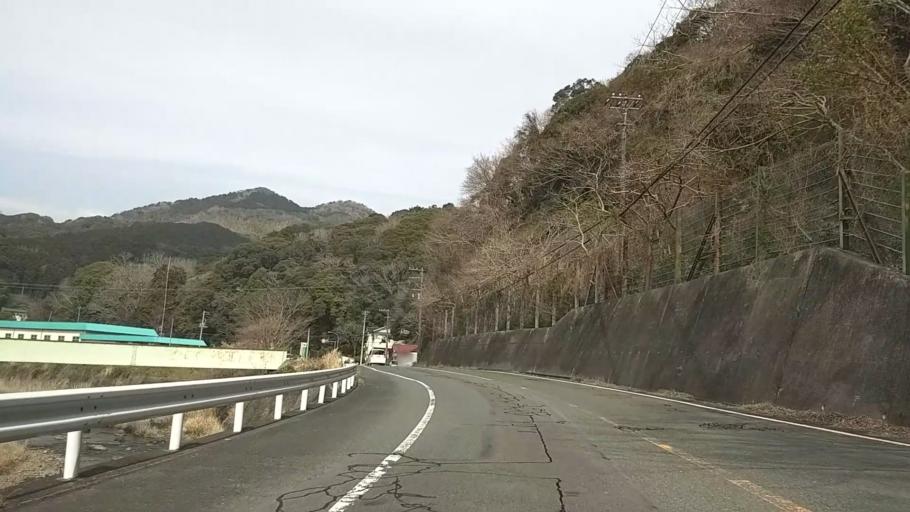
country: JP
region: Shizuoka
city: Shimoda
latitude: 34.7204
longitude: 138.9465
